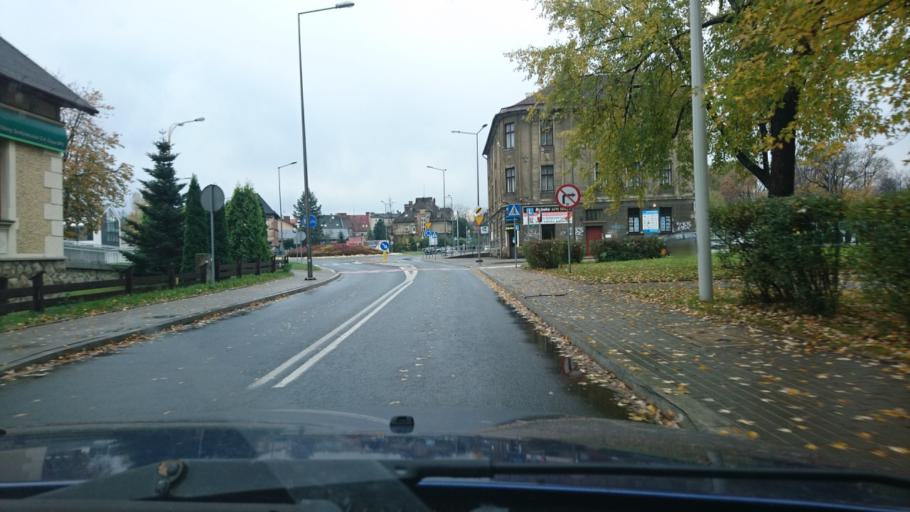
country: PL
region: Silesian Voivodeship
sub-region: Bielsko-Biala
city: Bielsko-Biala
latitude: 49.8164
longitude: 19.0478
